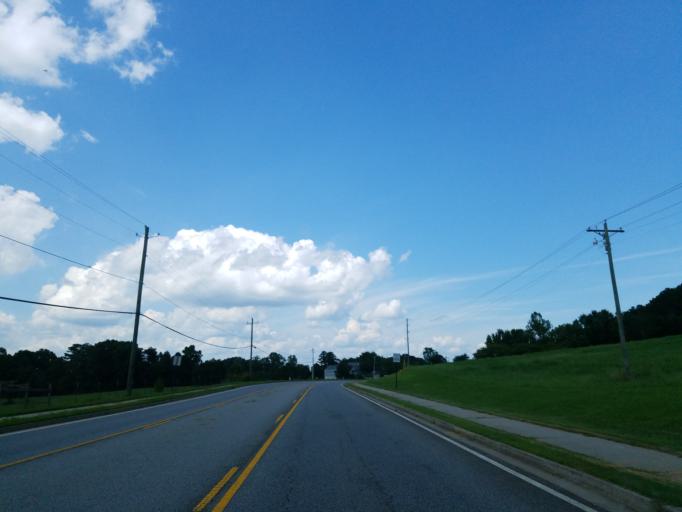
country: US
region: Georgia
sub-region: Forsyth County
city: Cumming
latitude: 34.2188
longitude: -84.1247
